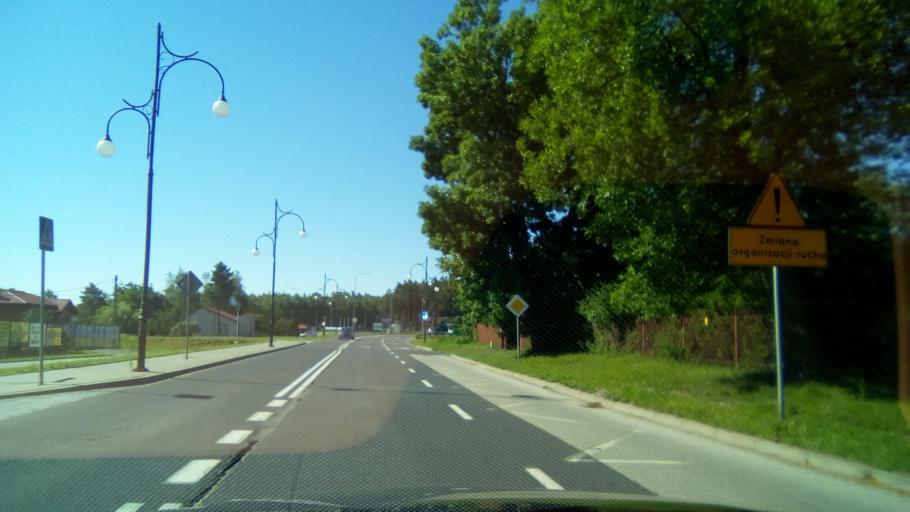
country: PL
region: Lodz Voivodeship
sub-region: Powiat lodzki wschodni
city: Rzgow
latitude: 51.6451
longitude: 19.4941
